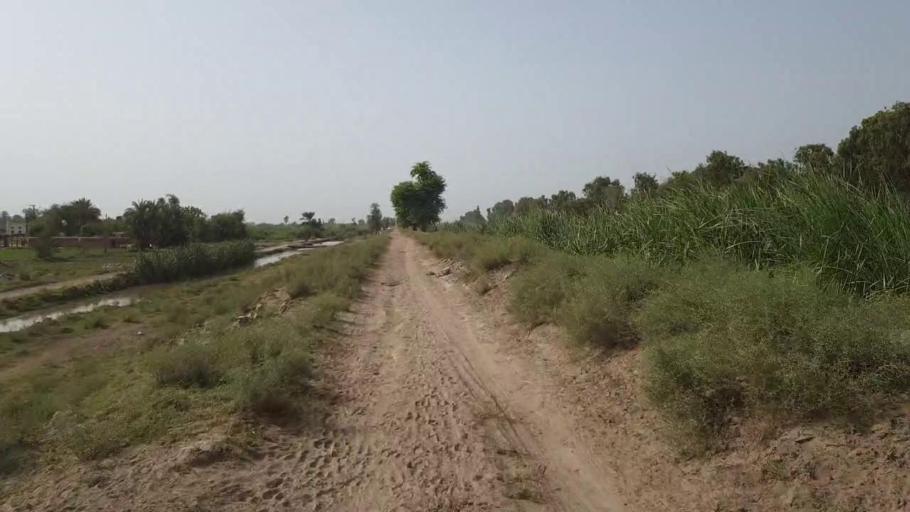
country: PK
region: Sindh
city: Daur
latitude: 26.4503
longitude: 68.1595
